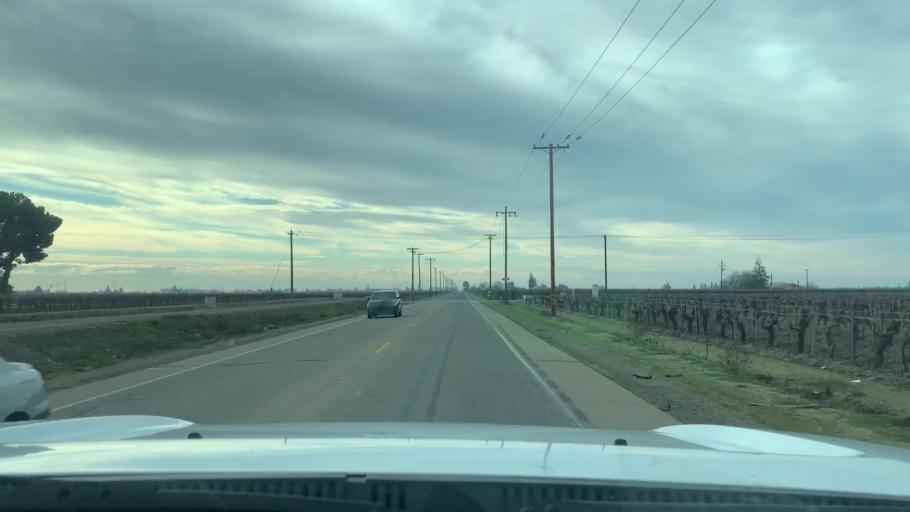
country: US
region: California
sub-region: Fresno County
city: Fowler
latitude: 36.6055
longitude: -119.7169
